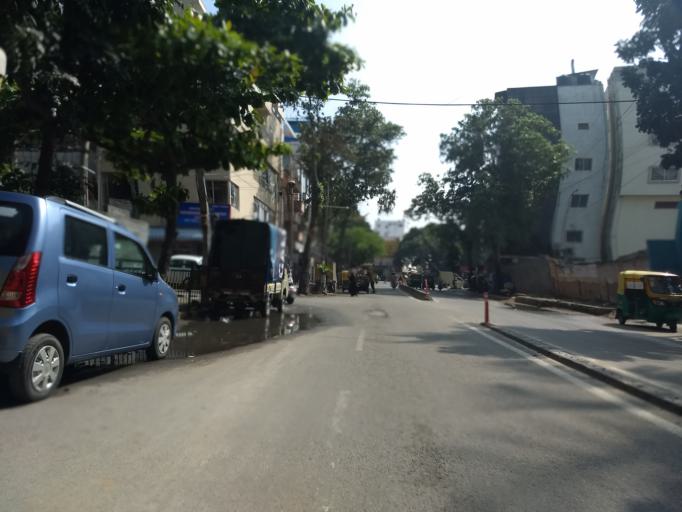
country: IN
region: Karnataka
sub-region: Bangalore Urban
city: Bangalore
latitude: 12.9611
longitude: 77.5873
